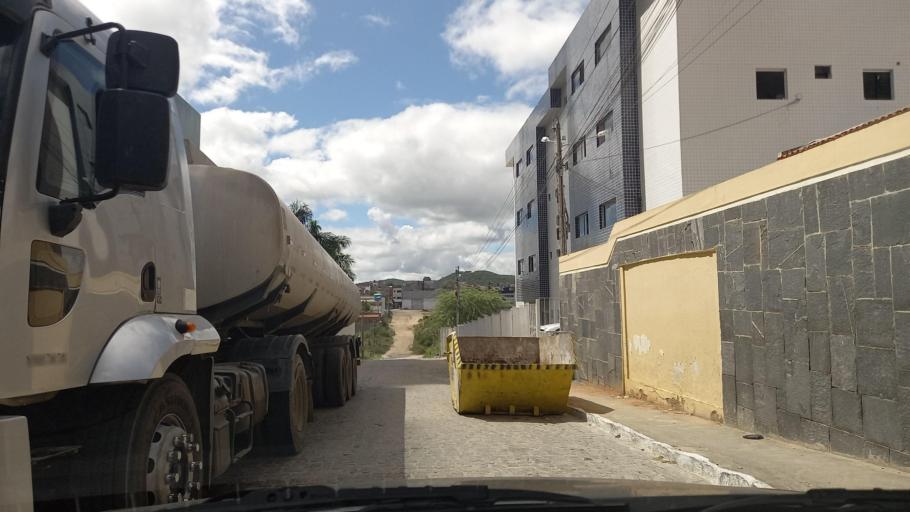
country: BR
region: Pernambuco
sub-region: Caruaru
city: Caruaru
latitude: -8.2656
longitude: -35.9635
